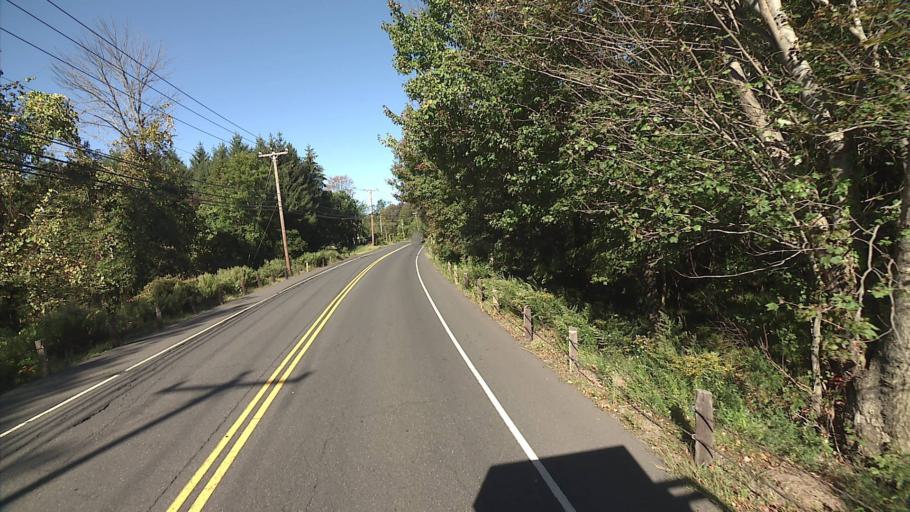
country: US
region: Connecticut
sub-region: New Haven County
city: Prospect
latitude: 41.5002
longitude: -72.9671
